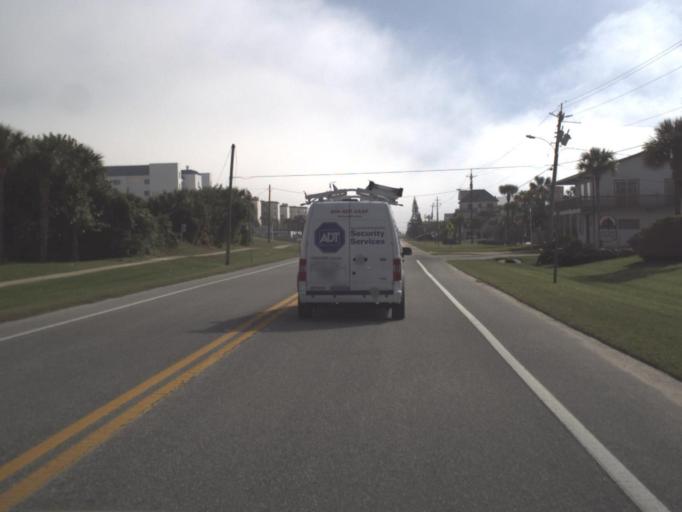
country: US
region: Florida
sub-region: Volusia County
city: Edgewater
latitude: 28.9515
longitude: -80.8407
